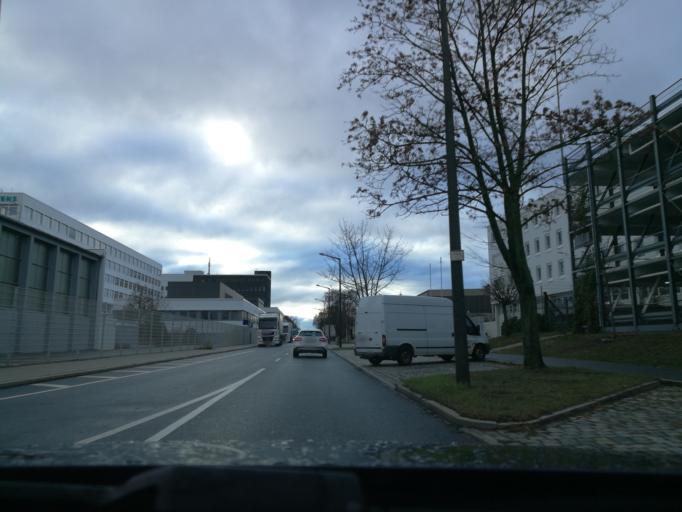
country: DE
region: Bavaria
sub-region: Regierungsbezirk Mittelfranken
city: Furth
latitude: 49.4815
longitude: 10.9634
